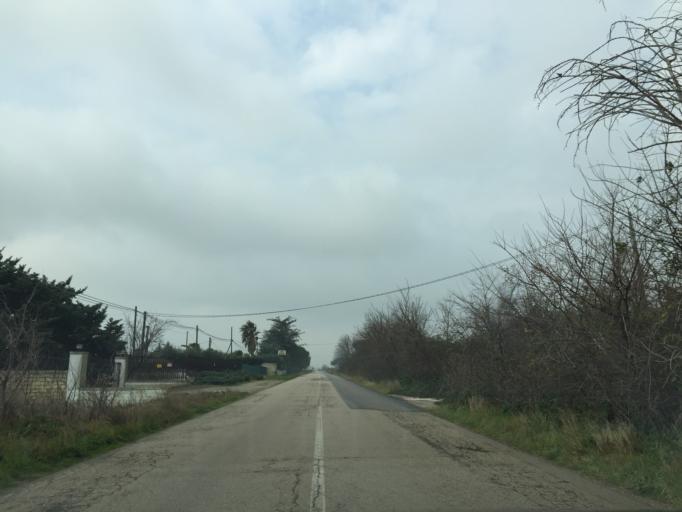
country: IT
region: Apulia
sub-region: Provincia di Foggia
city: Troia
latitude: 41.3819
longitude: 15.3763
